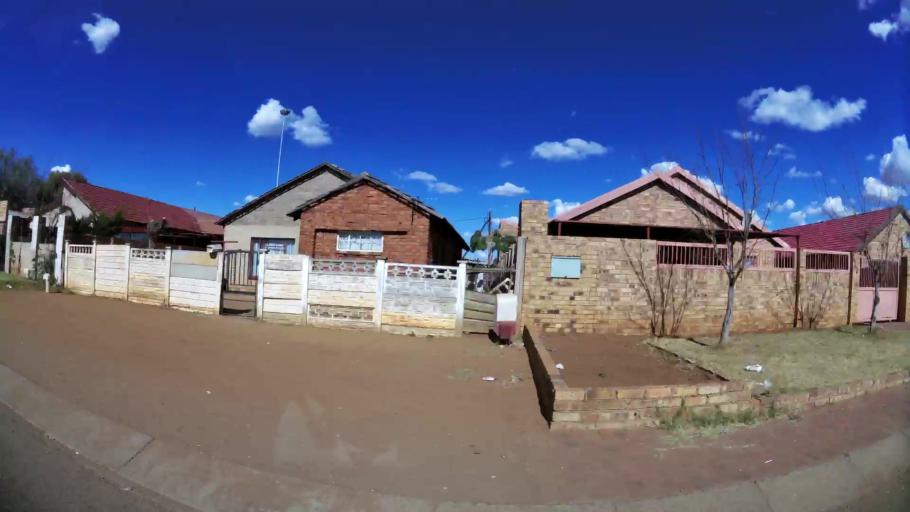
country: ZA
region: North-West
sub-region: Dr Kenneth Kaunda District Municipality
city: Klerksdorp
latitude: -26.8685
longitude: 26.5865
